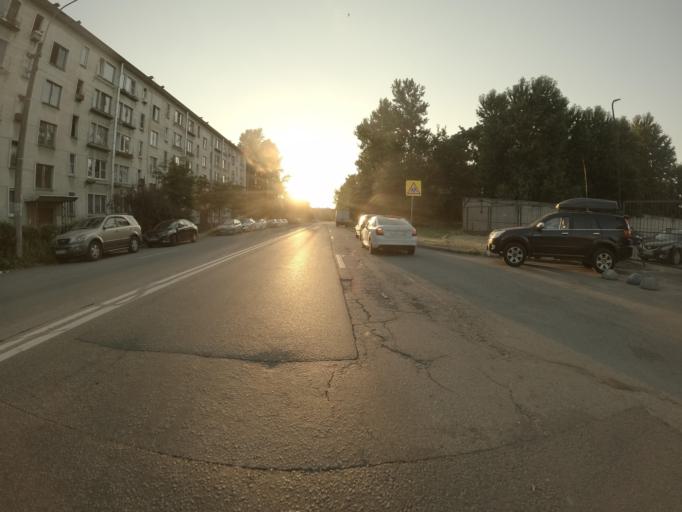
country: RU
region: St.-Petersburg
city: Avtovo
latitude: 59.8685
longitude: 30.2783
